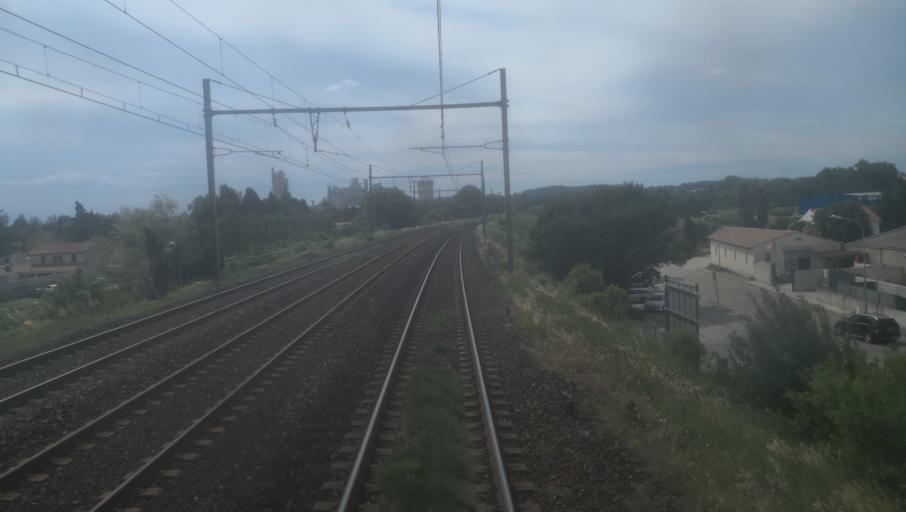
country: FR
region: Languedoc-Roussillon
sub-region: Departement du Gard
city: Beaucaire
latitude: 43.8035
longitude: 4.6358
